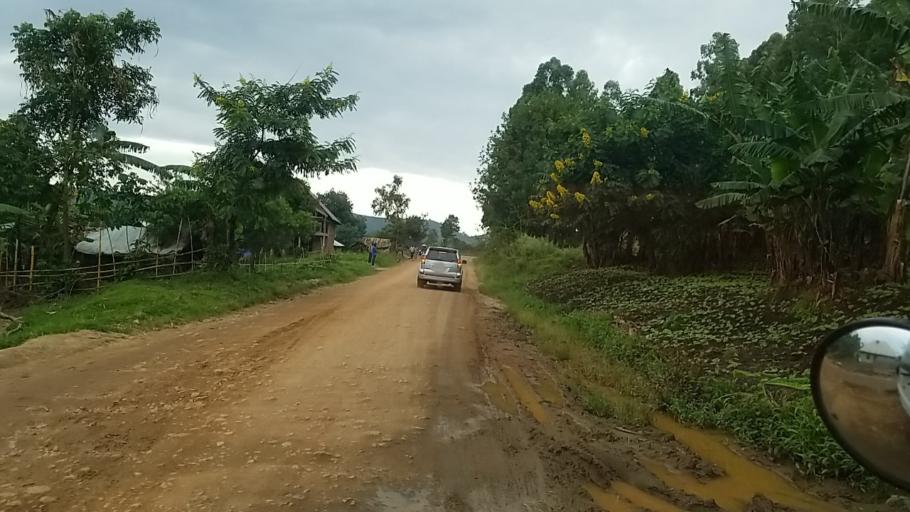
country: CD
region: Nord Kivu
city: Sake
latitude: -1.6723
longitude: 29.0177
